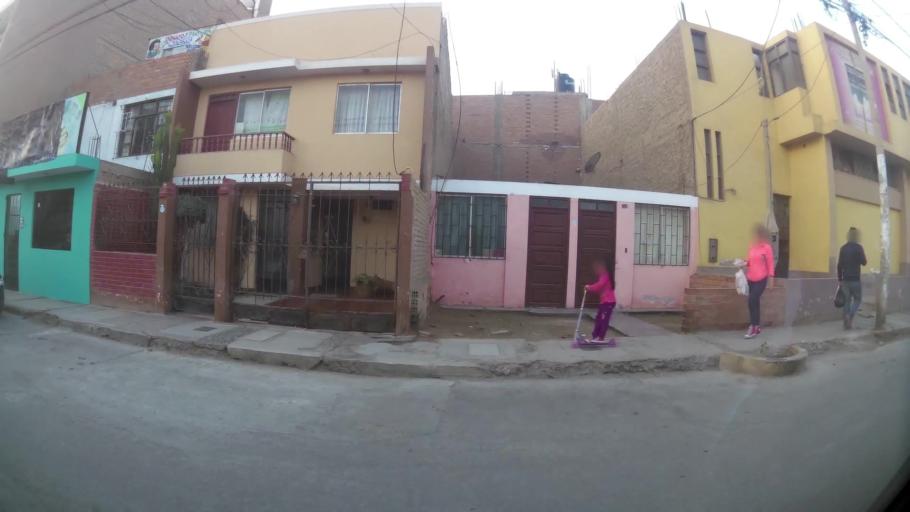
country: PE
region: Lima
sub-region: Huaura
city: Huacho
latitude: -11.1169
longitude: -77.6098
